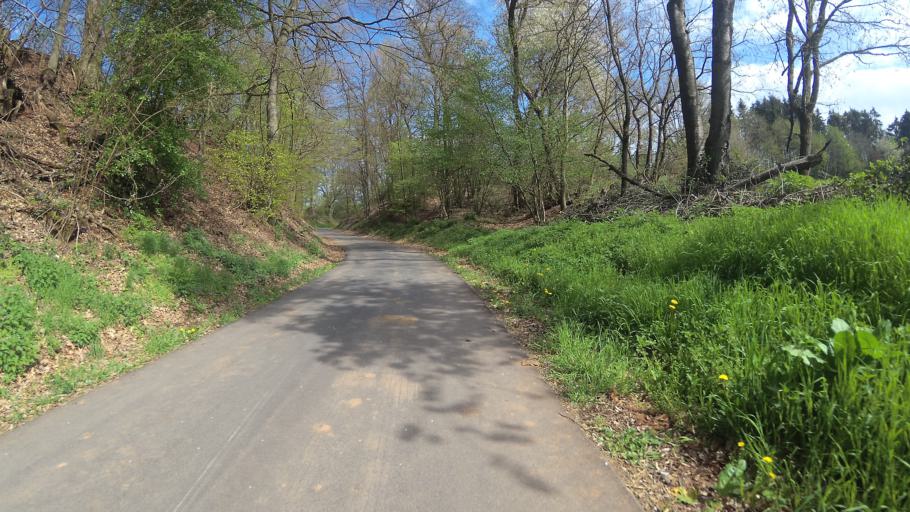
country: DE
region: Saarland
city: Mainzweiler
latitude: 49.4461
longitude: 7.1159
